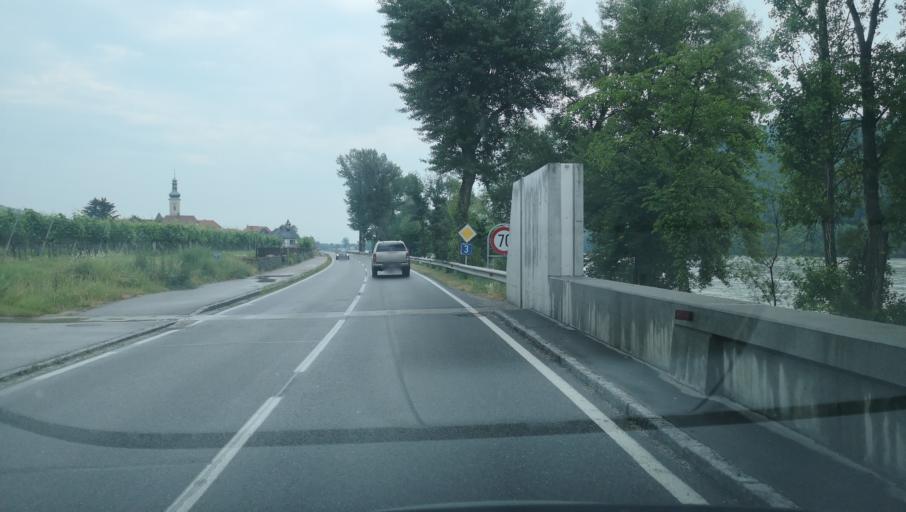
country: AT
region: Lower Austria
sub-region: Politischer Bezirk Krems
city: Durnstein
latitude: 48.3854
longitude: 15.5357
